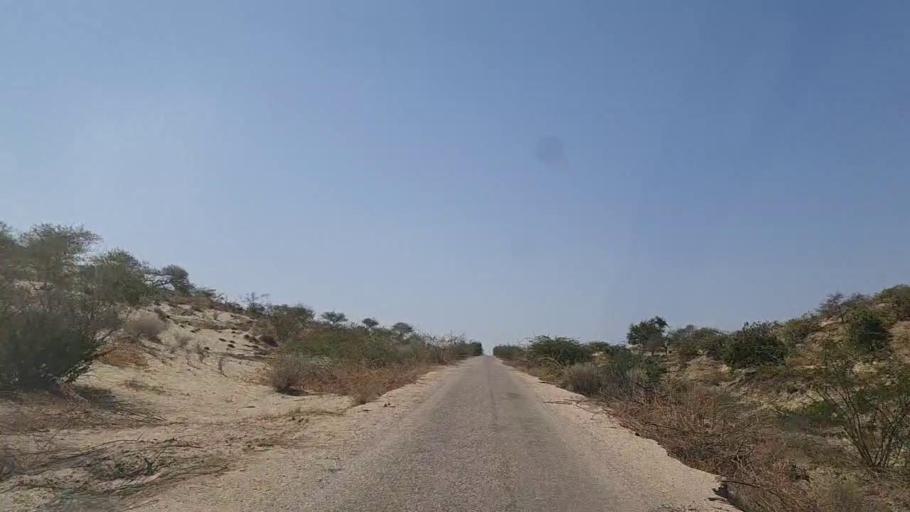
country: PK
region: Sindh
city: Diplo
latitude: 24.5334
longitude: 69.3850
